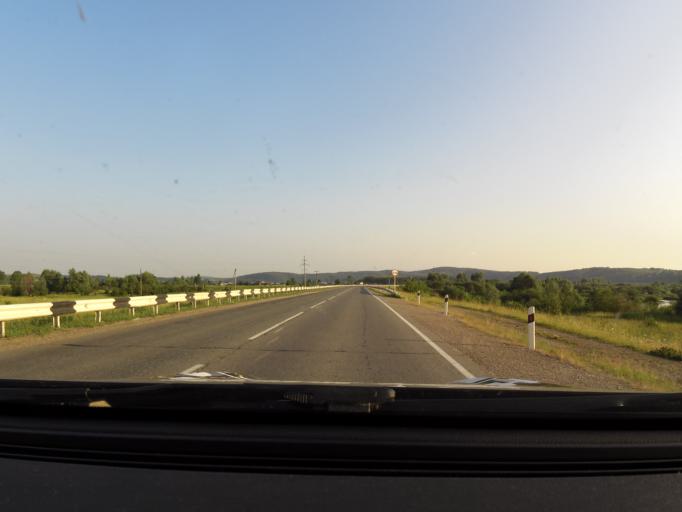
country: RU
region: Sverdlovsk
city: Mikhaylovsk
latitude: 56.4351
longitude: 59.0847
